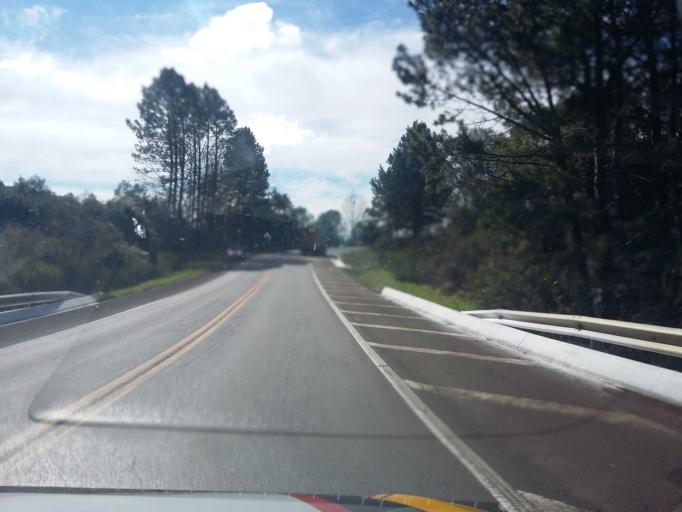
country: BR
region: Rio Grande do Sul
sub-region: Vacaria
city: Vacaria
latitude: -28.5726
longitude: -51.0137
